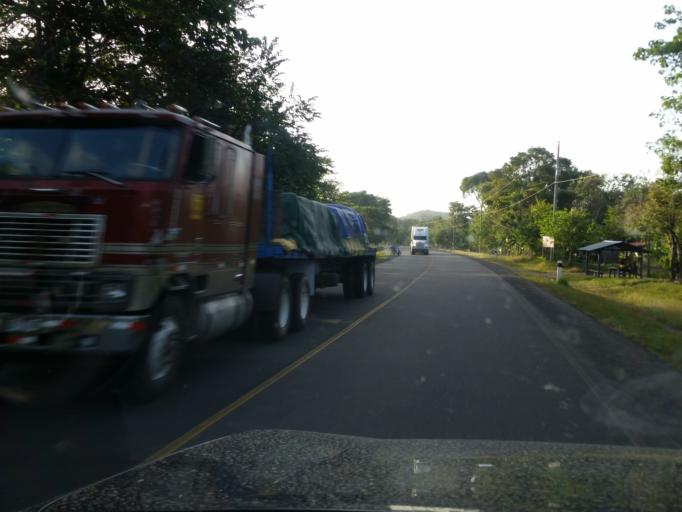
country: NI
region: Rio San Juan
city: San Miguelito
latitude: 11.3950
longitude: -84.8052
